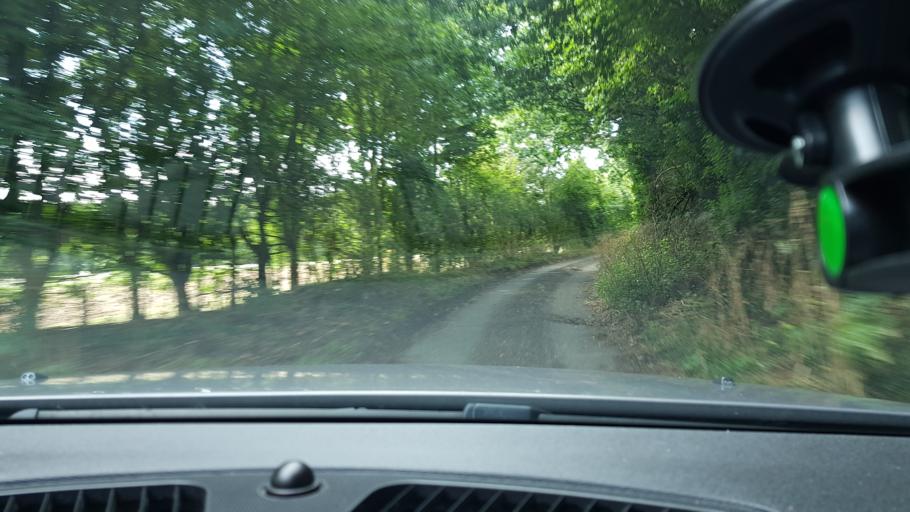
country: GB
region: England
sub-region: West Berkshire
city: Kintbury
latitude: 51.4284
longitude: -1.4606
